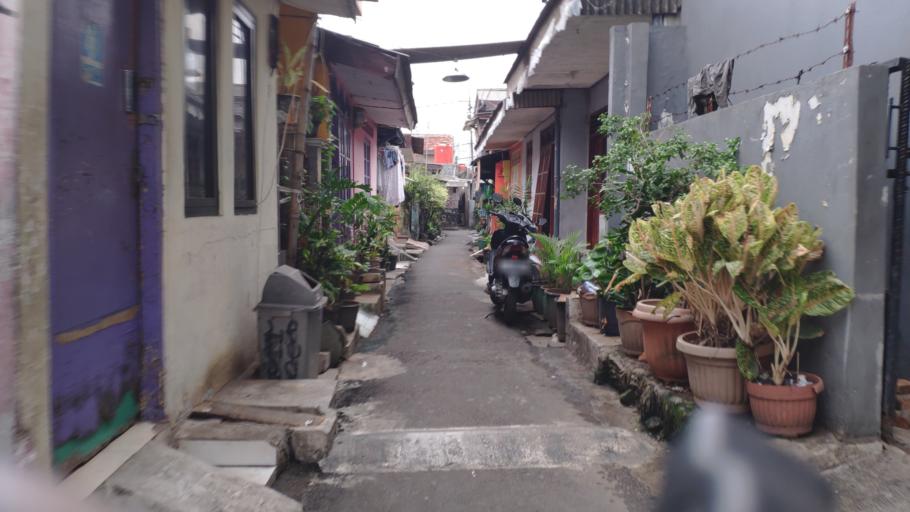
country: ID
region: Jakarta Raya
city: Jakarta
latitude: -6.2163
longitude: 106.8399
